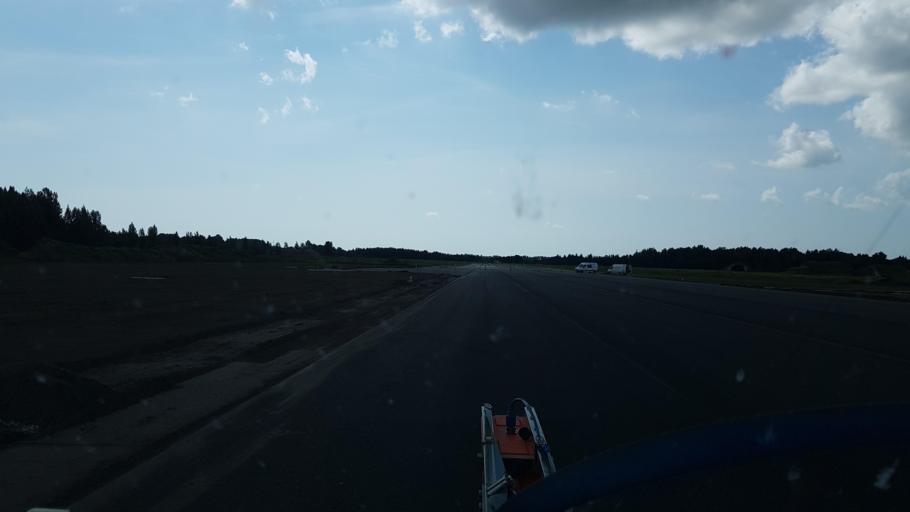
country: EE
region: Paernumaa
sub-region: Sauga vald
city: Sauga
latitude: 58.4147
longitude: 24.4679
